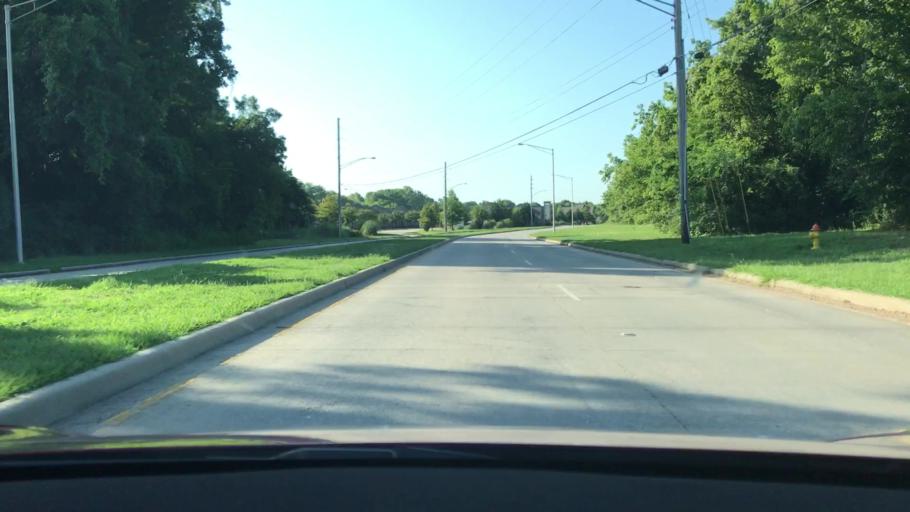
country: US
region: Louisiana
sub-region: Bossier Parish
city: Bossier City
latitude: 32.4352
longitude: -93.7276
